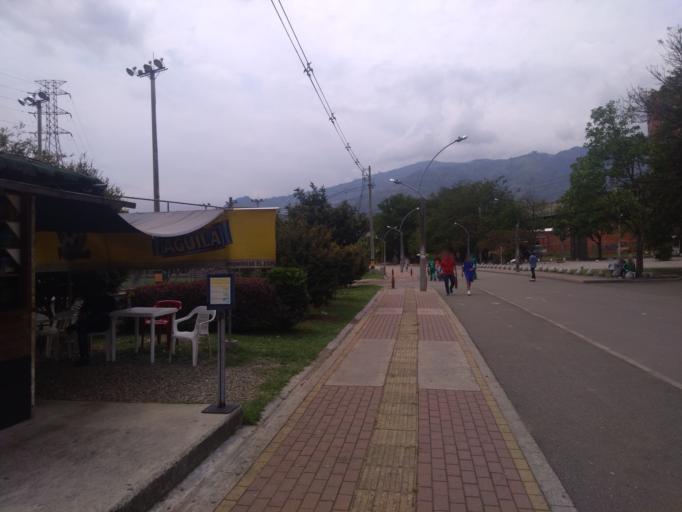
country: CO
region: Antioquia
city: Bello
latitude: 6.3364
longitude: -75.5468
